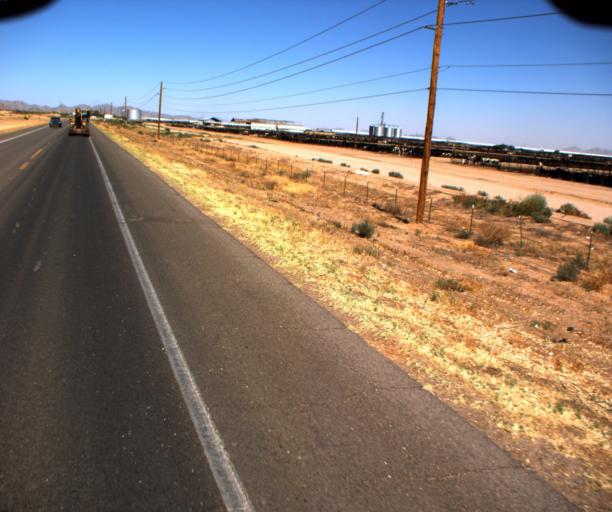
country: US
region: Arizona
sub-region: Pinal County
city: Maricopa
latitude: 32.8794
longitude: -112.0097
